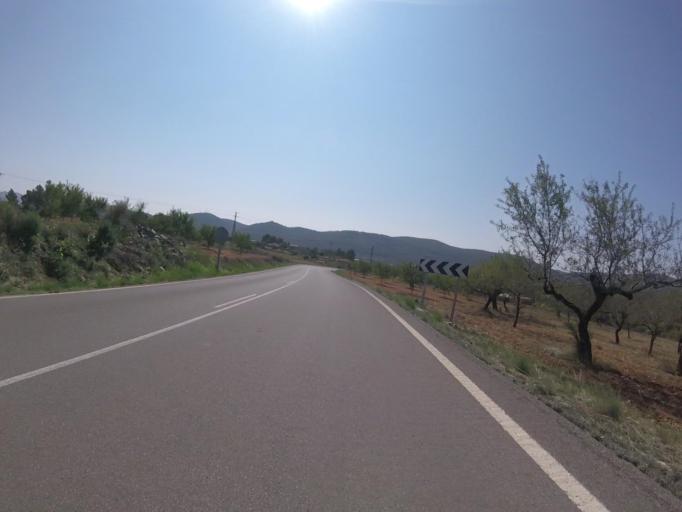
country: ES
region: Valencia
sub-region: Provincia de Castello
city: Adzaneta
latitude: 40.2277
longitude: -0.1742
